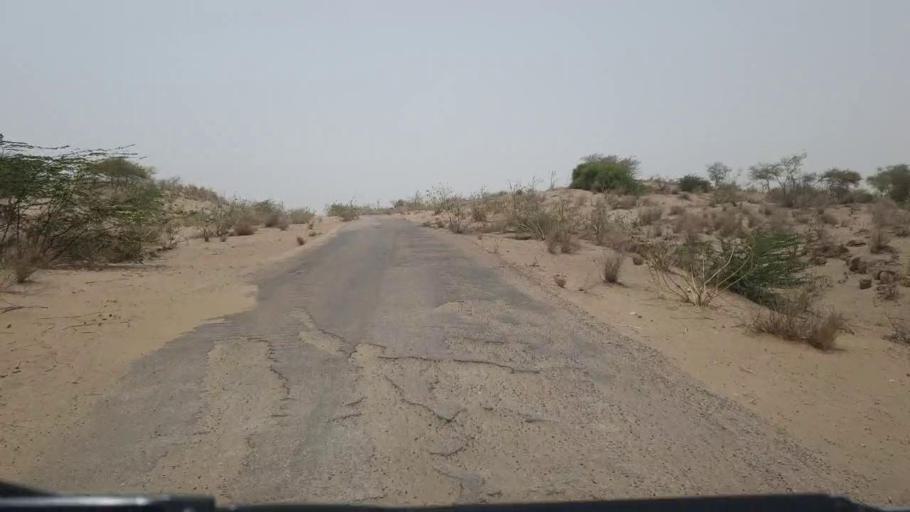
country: PK
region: Sindh
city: Naukot
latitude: 24.7788
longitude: 69.5363
